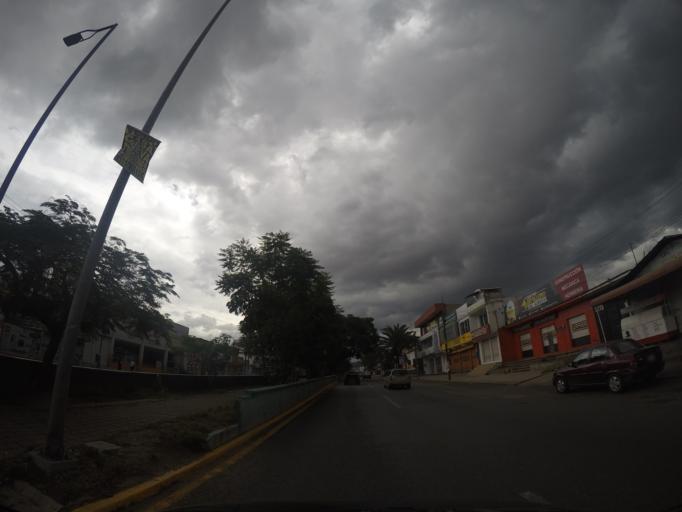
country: MX
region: Oaxaca
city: Oaxaca de Juarez
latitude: 17.0695
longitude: -96.7023
